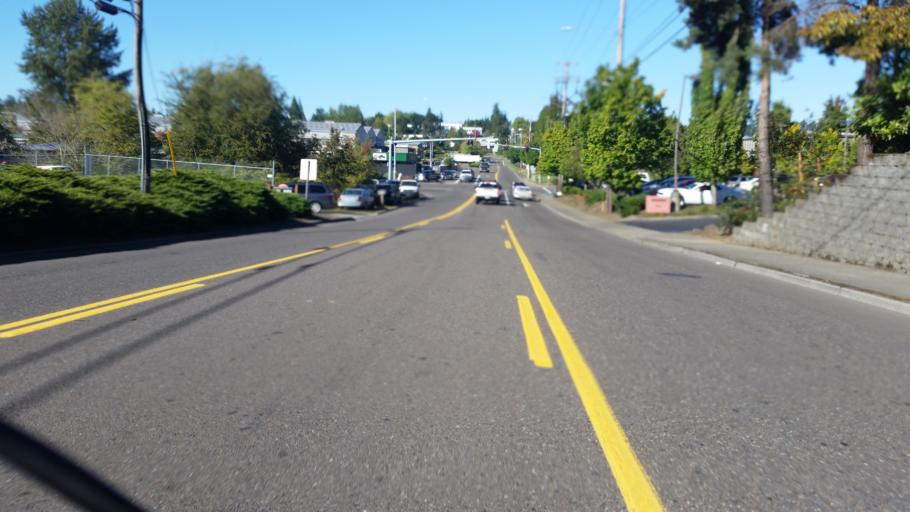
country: US
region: Oregon
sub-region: Washington County
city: Durham
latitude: 45.4143
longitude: -122.7491
